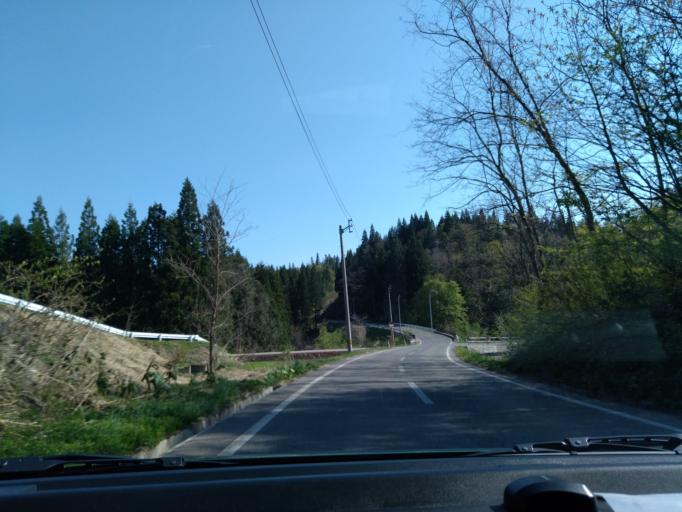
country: JP
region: Akita
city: Yokotemachi
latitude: 39.3767
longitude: 140.5838
